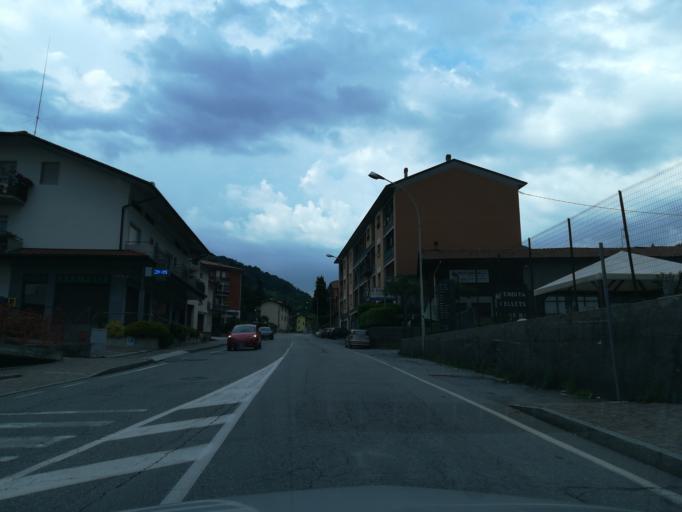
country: IT
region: Lombardy
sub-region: Provincia di Bergamo
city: Almenno San Salvatore
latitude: 45.7514
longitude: 9.5990
